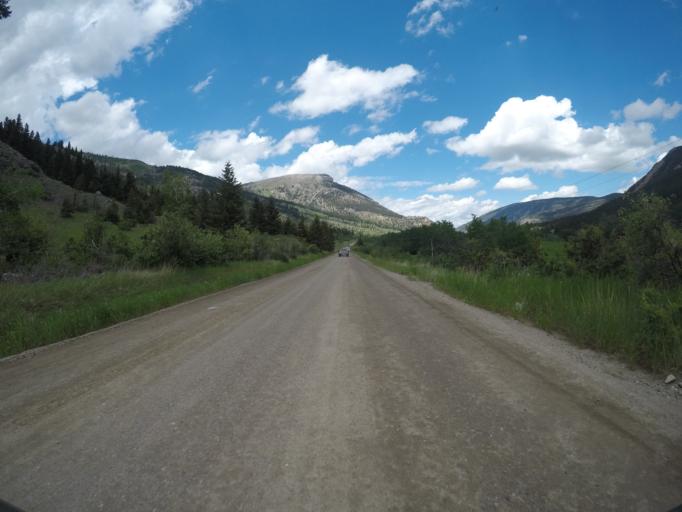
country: US
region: Montana
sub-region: Park County
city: Livingston
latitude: 45.5136
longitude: -110.2268
